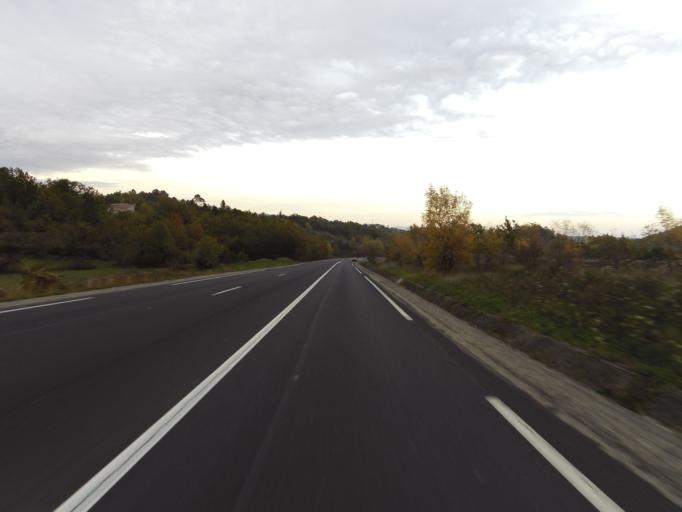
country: FR
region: Rhone-Alpes
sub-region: Departement de l'Ardeche
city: Lablachere
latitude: 44.4680
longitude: 4.2302
